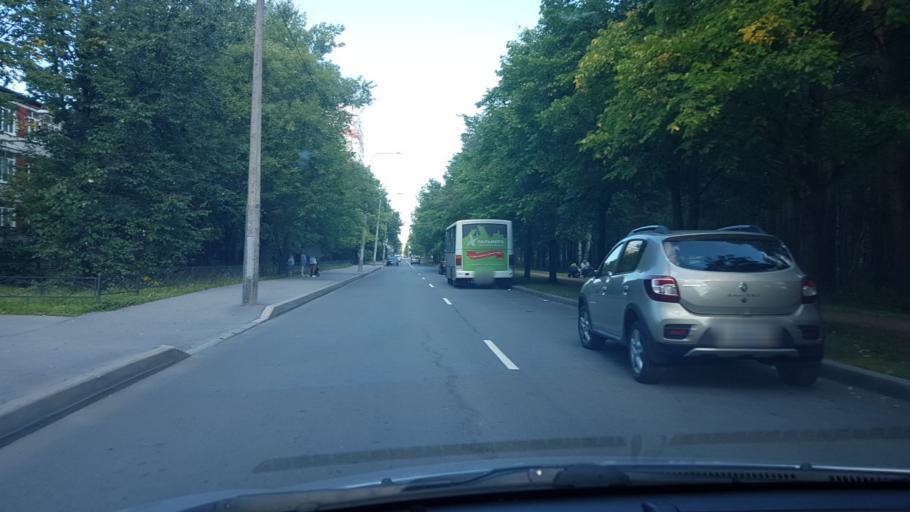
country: RU
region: St.-Petersburg
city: Dachnoye
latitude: 59.8316
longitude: 30.2262
